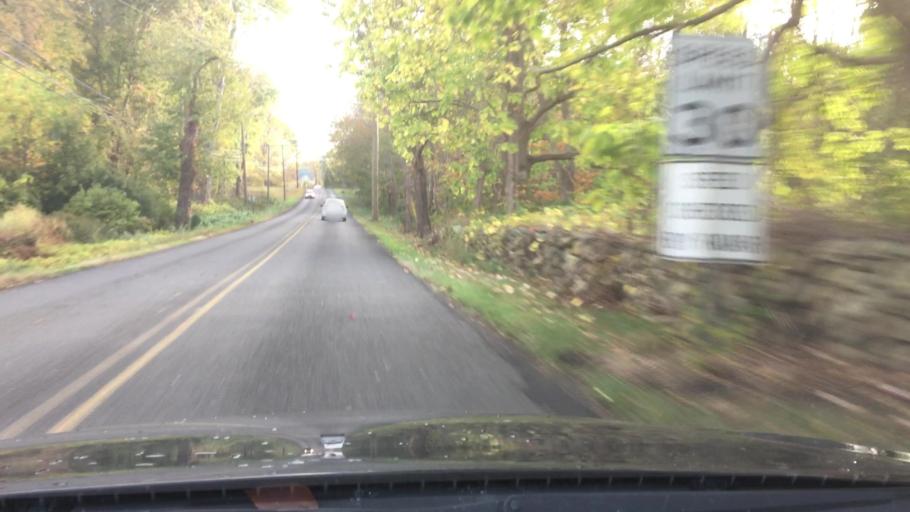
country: US
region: Connecticut
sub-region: Litchfield County
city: New Milford
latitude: 41.5522
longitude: -73.3164
